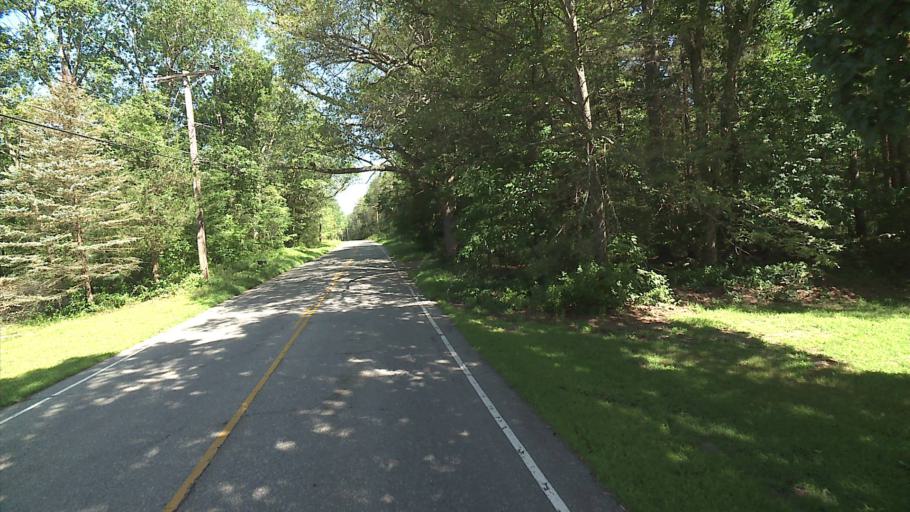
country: US
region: Connecticut
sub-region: New London County
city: Baltic
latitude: 41.6802
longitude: -72.0844
